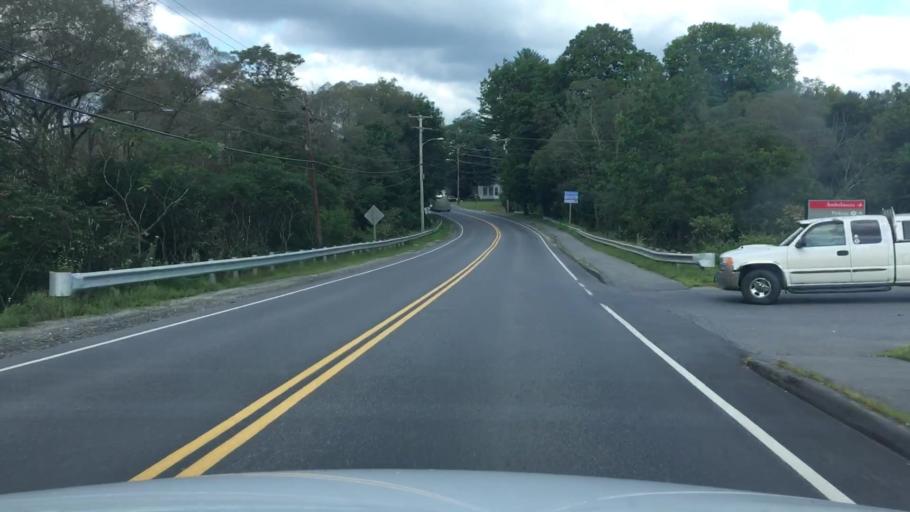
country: US
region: Maine
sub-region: Somerset County
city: Skowhegan
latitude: 44.7592
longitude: -69.7144
